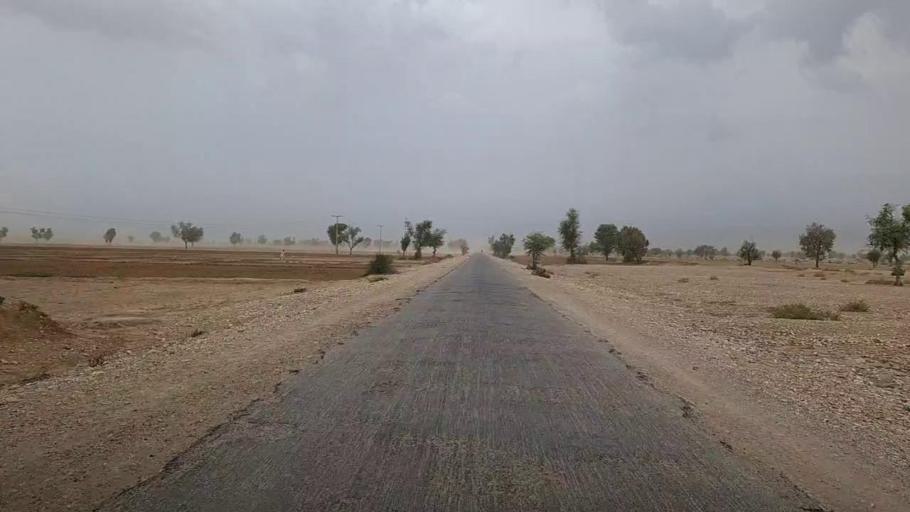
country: PK
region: Sindh
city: Sehwan
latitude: 26.3180
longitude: 67.7305
